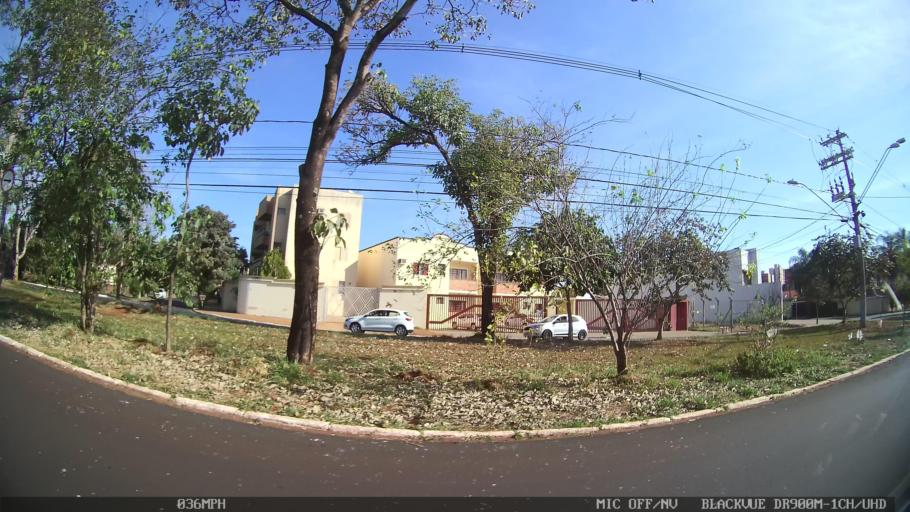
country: BR
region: Sao Paulo
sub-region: Ribeirao Preto
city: Ribeirao Preto
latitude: -21.1885
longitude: -47.7676
